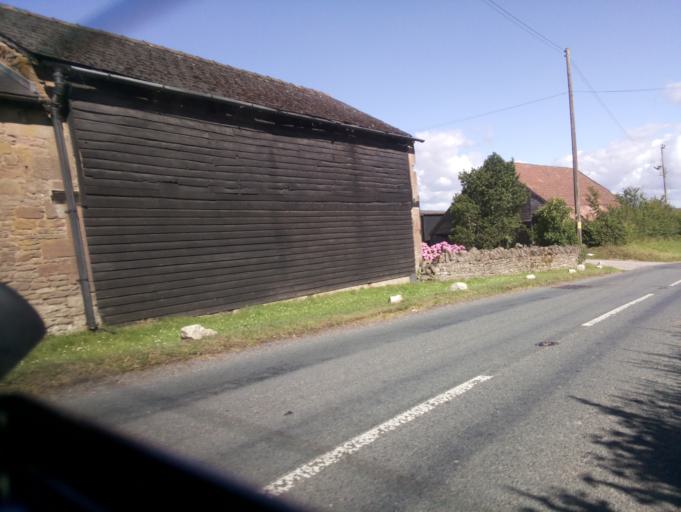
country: GB
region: England
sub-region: Herefordshire
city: Yatton
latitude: 51.9665
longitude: -2.5512
